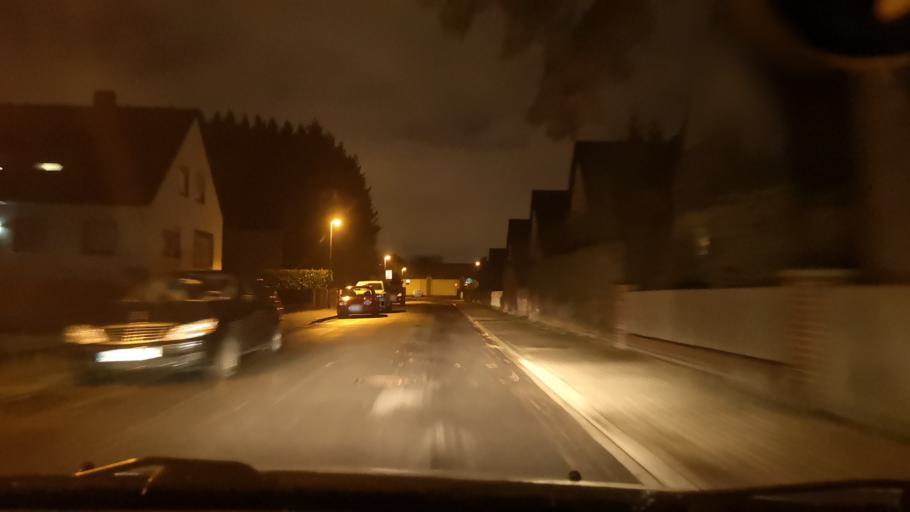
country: DE
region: Lower Saxony
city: Langenhagen
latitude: 52.4292
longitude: 9.7373
